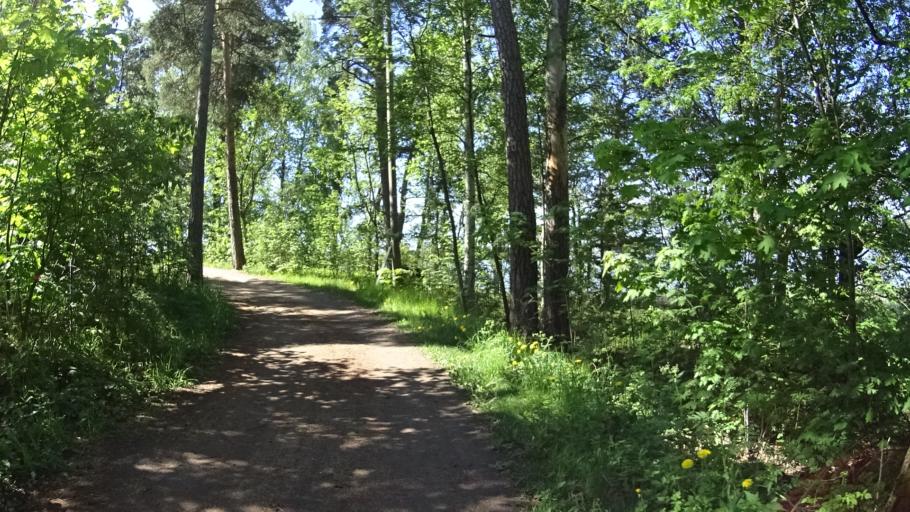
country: FI
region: Uusimaa
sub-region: Helsinki
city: Teekkarikylae
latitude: 60.1779
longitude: 24.8475
